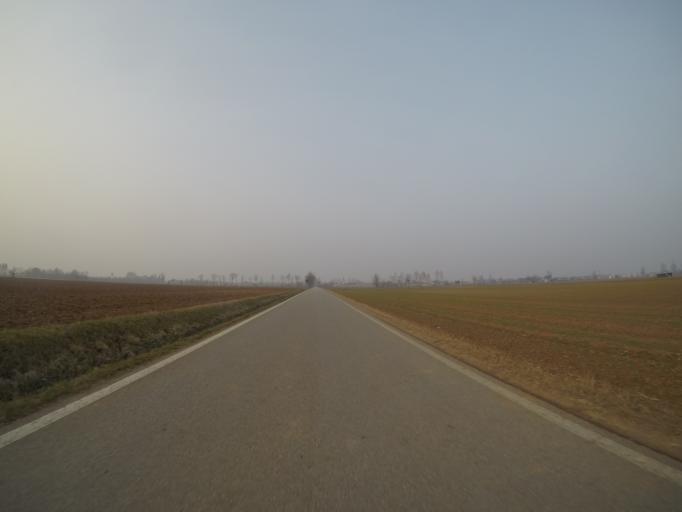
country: IT
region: Veneto
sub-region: Provincia di Treviso
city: Altivole
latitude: 45.7410
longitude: 11.9598
